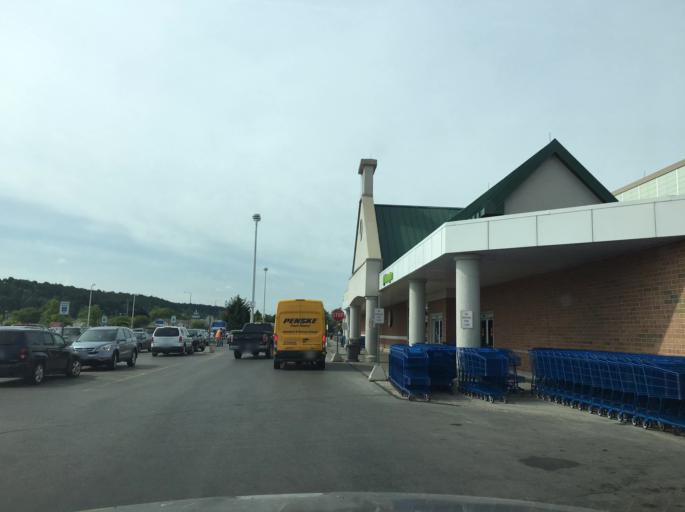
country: US
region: Michigan
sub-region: Grand Traverse County
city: Traverse City
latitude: 44.7430
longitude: -85.6439
